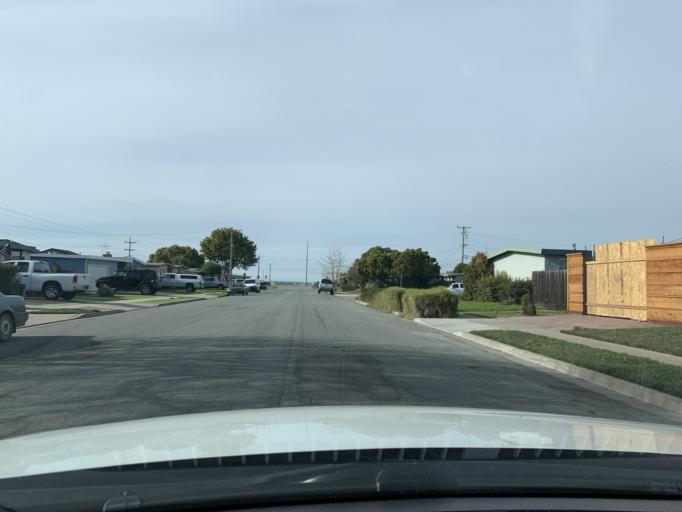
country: US
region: California
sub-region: Monterey County
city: Salinas
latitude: 36.6735
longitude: -121.6768
